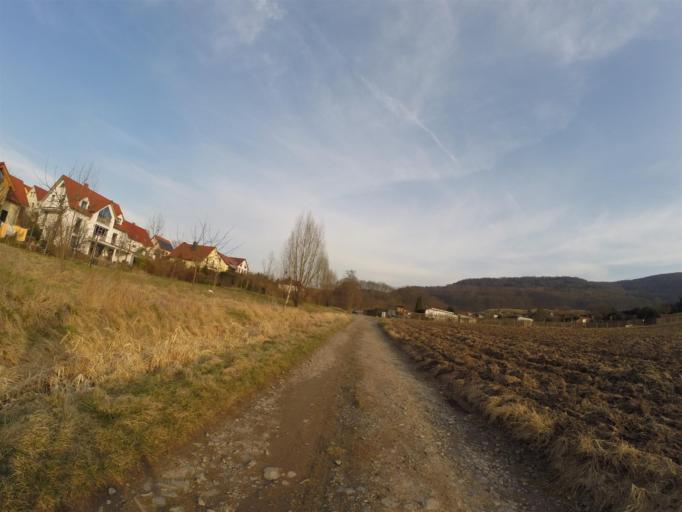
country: DE
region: Thuringia
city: Golmsdorf
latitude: 50.9515
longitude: 11.6387
